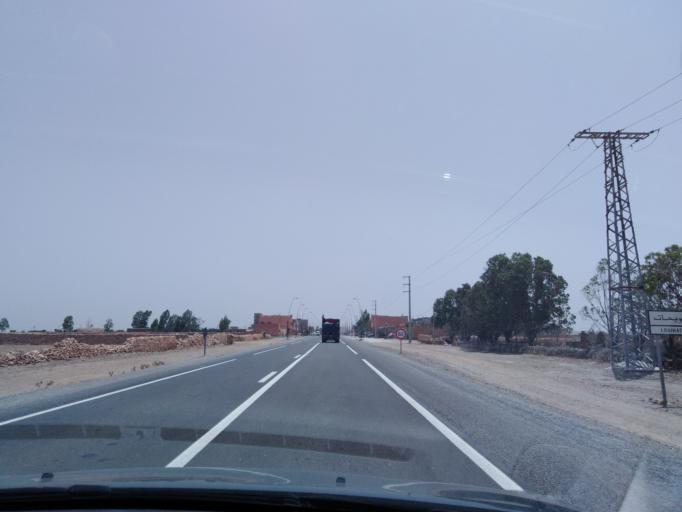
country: MA
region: Doukkala-Abda
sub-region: Safi
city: Youssoufia
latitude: 31.9857
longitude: -8.3739
